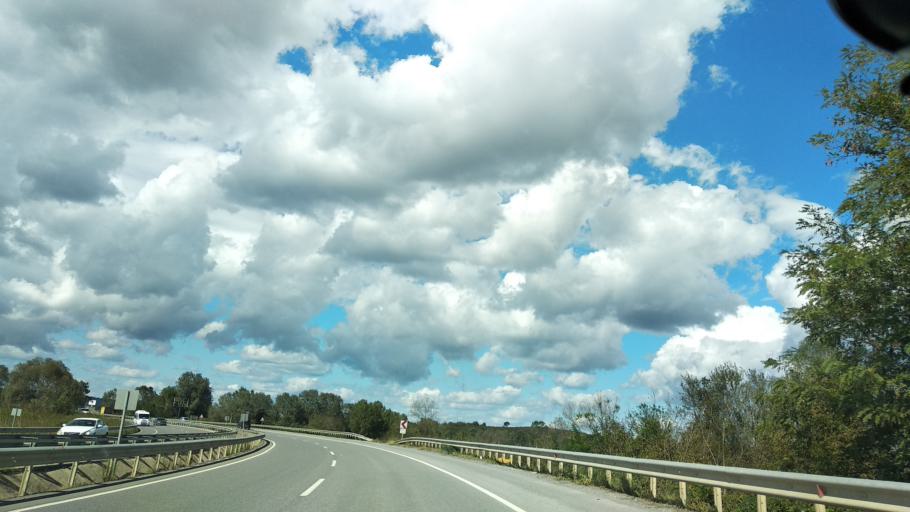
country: TR
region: Sakarya
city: Ferizli
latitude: 40.9616
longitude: 30.5108
